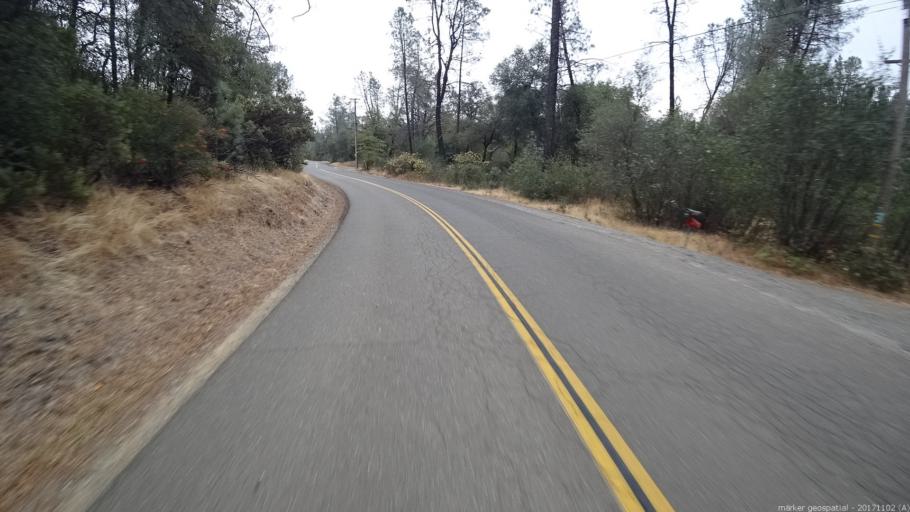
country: US
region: California
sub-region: Shasta County
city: Central Valley (historical)
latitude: 40.6627
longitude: -122.4011
